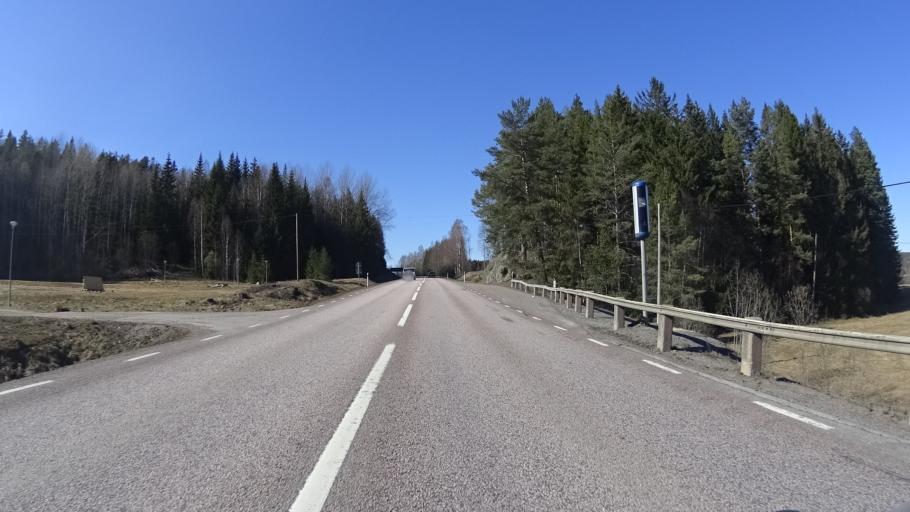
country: SE
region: Vaermland
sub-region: Karlstads Kommun
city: Edsvalla
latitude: 59.5340
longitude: 13.1105
